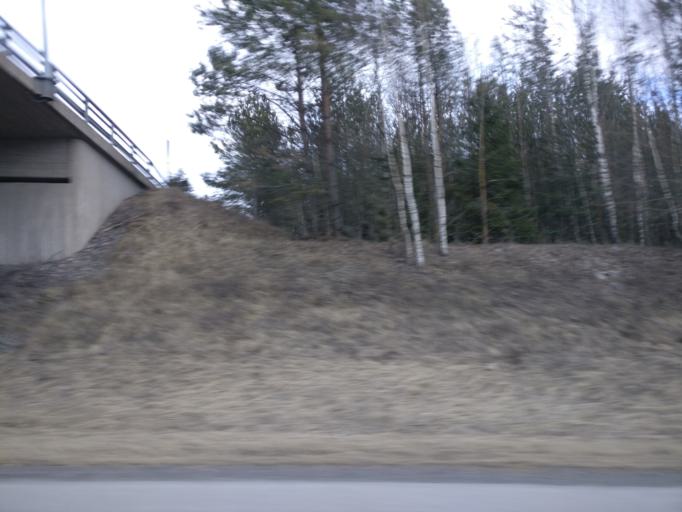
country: FI
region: Haeme
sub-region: Haemeenlinna
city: Janakkala
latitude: 60.8795
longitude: 24.5727
